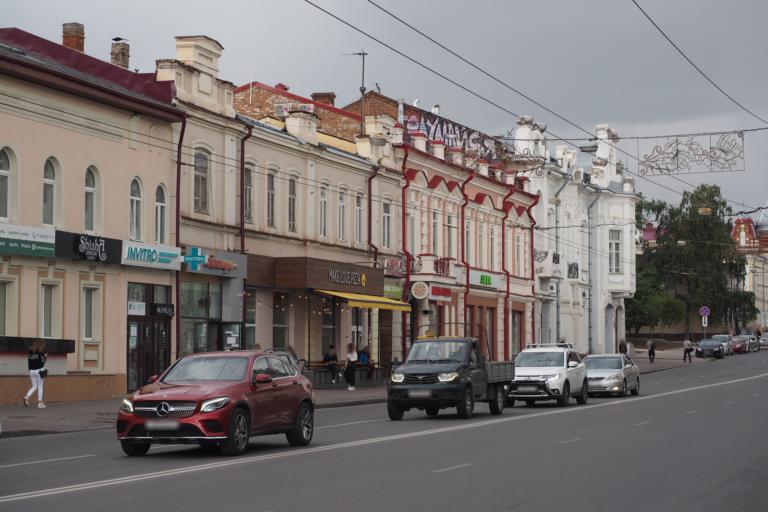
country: RU
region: Tomsk
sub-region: Tomskiy Rayon
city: Tomsk
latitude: 56.4788
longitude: 84.9498
